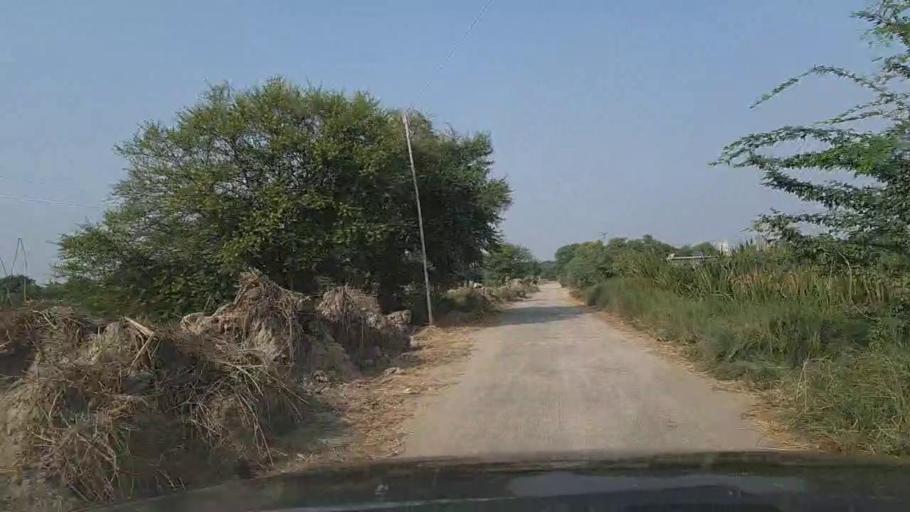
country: PK
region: Sindh
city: Mirpur Batoro
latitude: 24.7067
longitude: 68.2544
